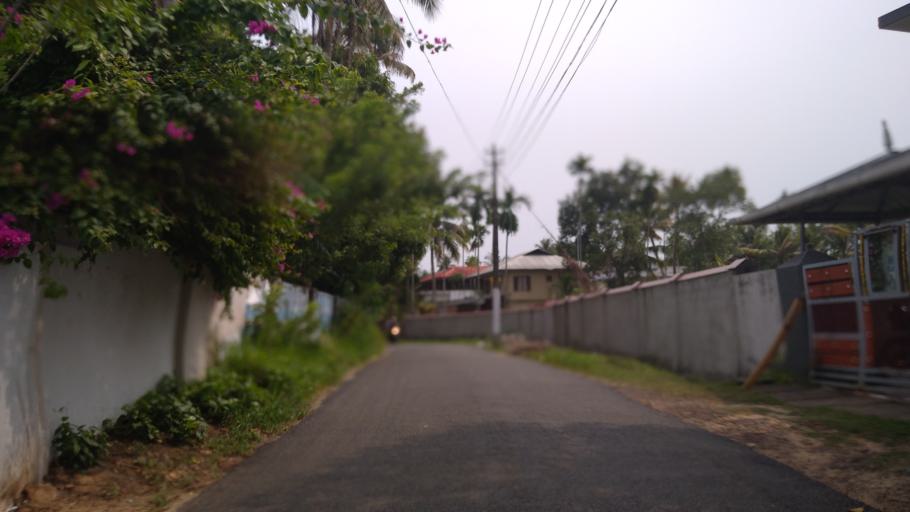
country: IN
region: Kerala
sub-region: Ernakulam
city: Elur
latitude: 10.1484
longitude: 76.2547
